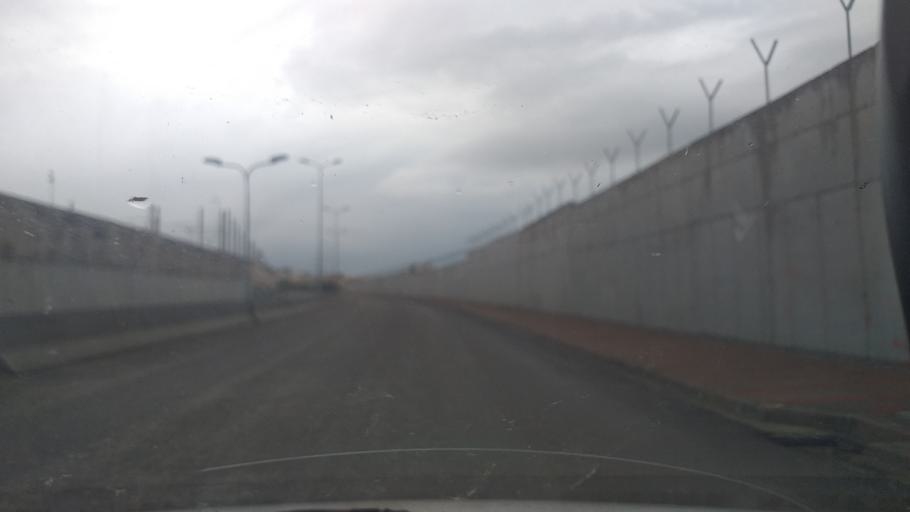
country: TN
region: Ariana
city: Ariana
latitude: 36.8571
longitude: 10.2136
